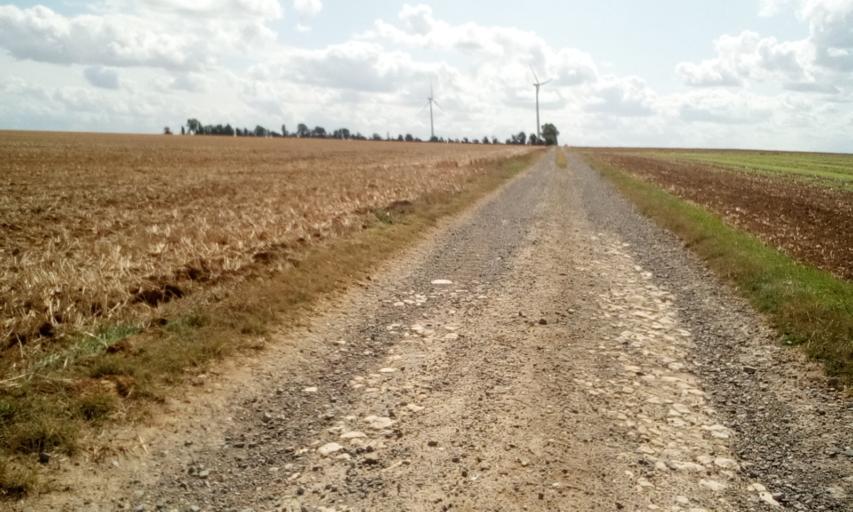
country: FR
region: Lower Normandy
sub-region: Departement du Calvados
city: Bellengreville
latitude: 49.1038
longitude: -0.2200
